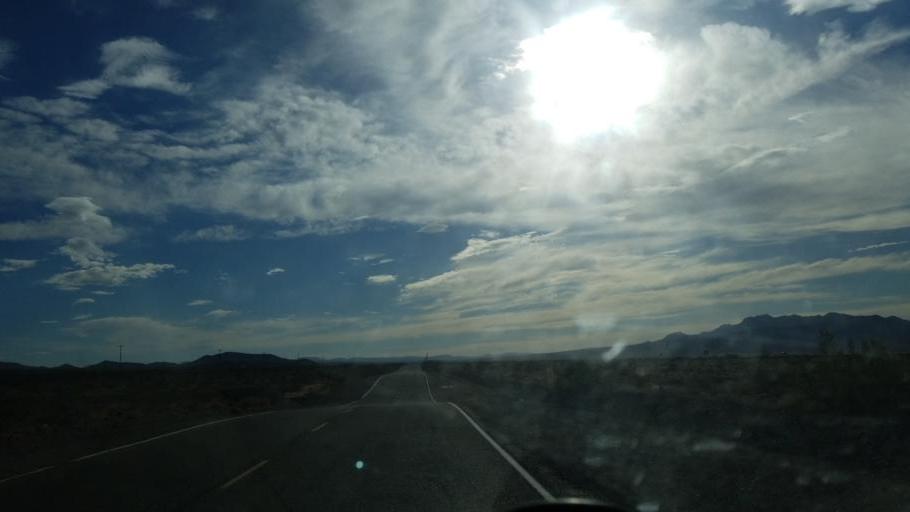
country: US
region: California
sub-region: San Bernardino County
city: Twentynine Palms
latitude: 34.7248
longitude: -116.1348
